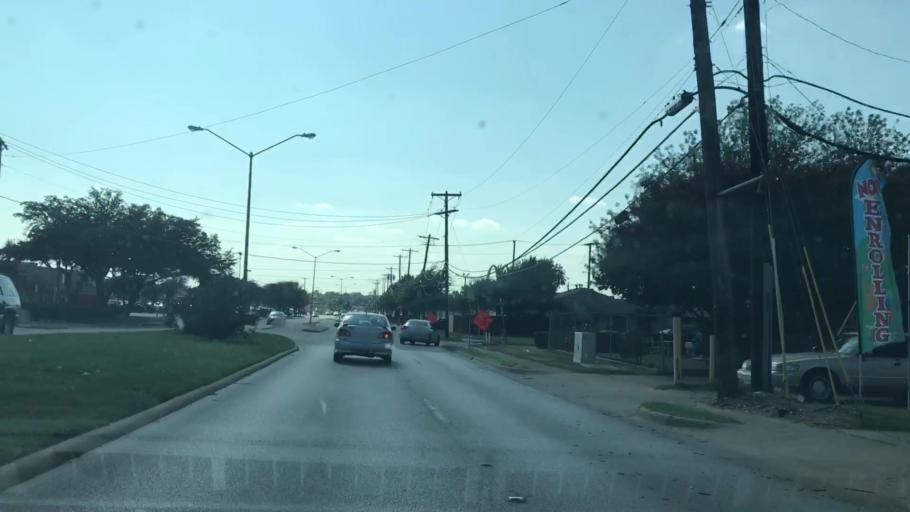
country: US
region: Texas
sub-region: Dallas County
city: Garland
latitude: 32.8349
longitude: -96.6697
